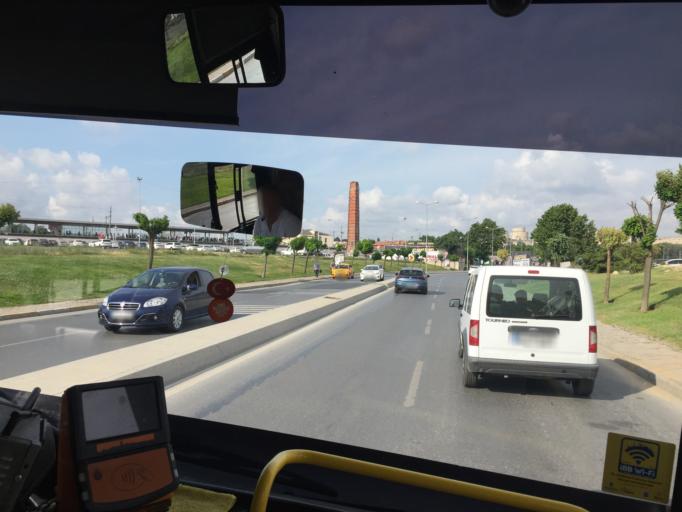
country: TR
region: Istanbul
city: Zeytinburnu
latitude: 40.9909
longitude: 28.9161
